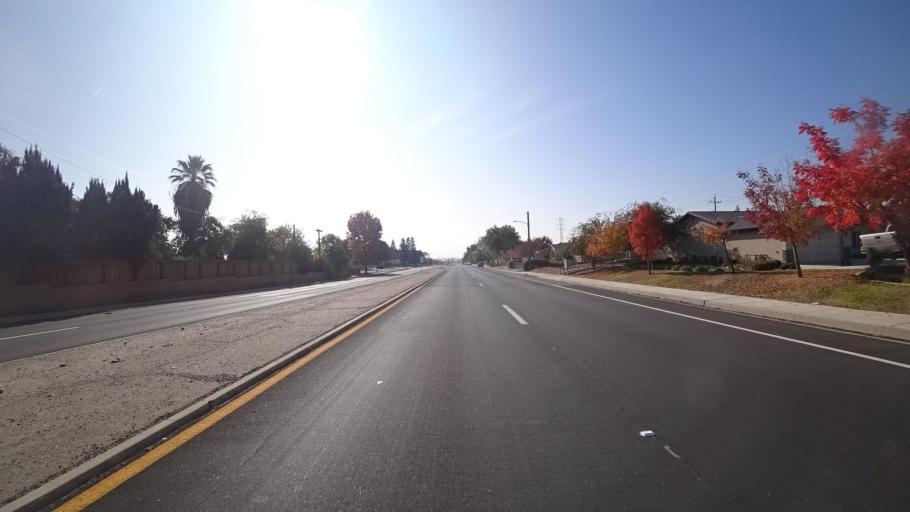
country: US
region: California
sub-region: Kern County
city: Oildale
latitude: 35.4347
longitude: -119.0124
